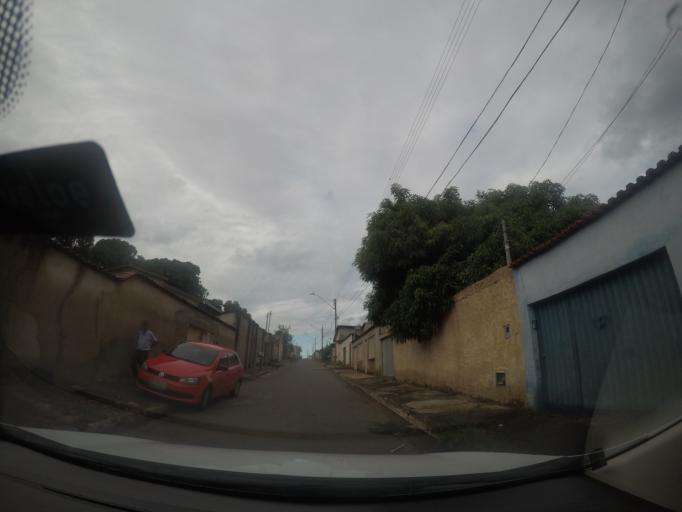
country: BR
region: Goias
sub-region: Goiania
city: Goiania
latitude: -16.6074
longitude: -49.3185
